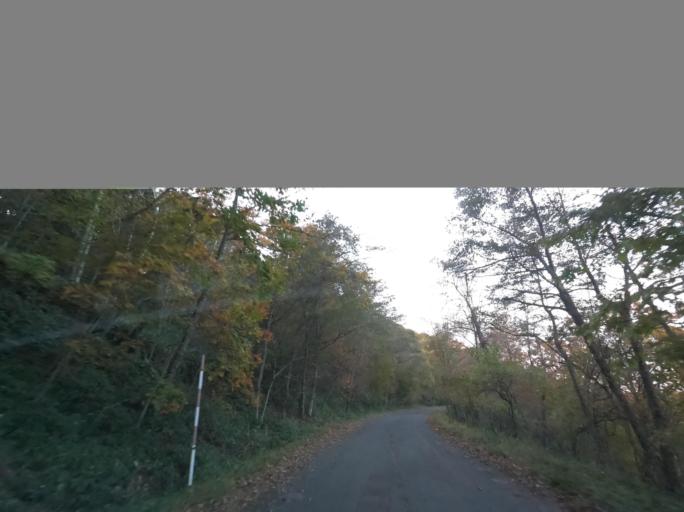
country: JP
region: Hokkaido
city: Kushiro
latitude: 43.1957
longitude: 144.4615
